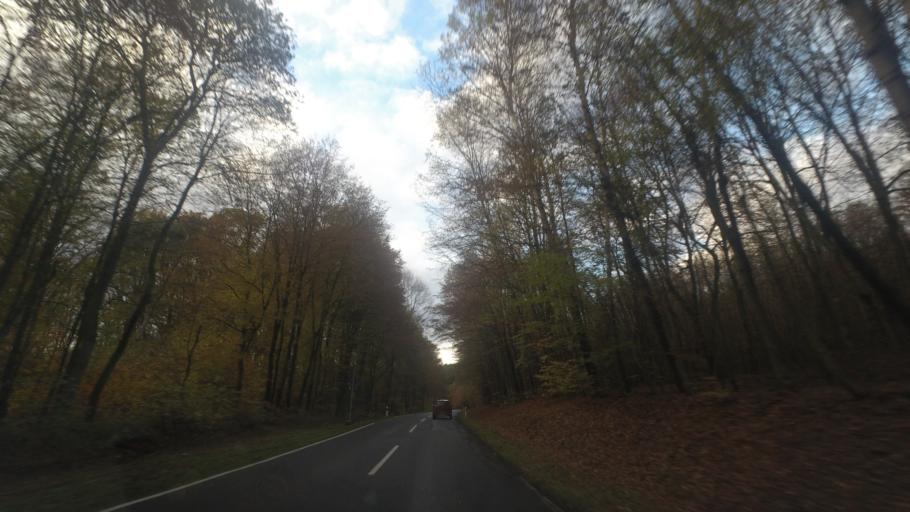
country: DE
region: Hesse
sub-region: Regierungsbezirk Kassel
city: Flieden
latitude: 50.4585
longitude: 9.5424
